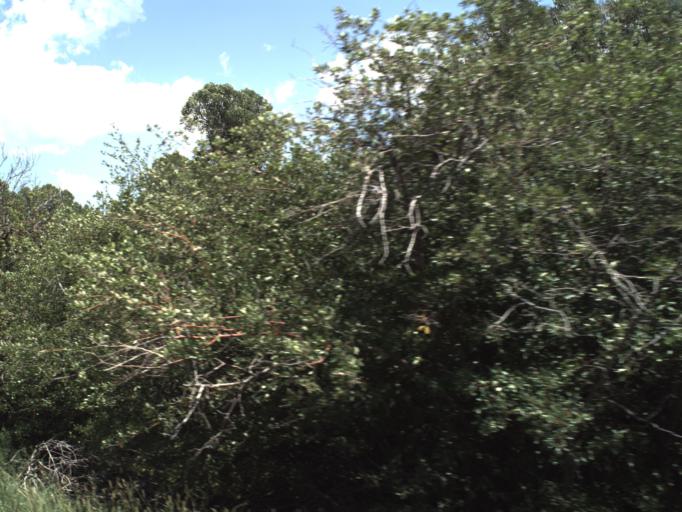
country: US
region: Utah
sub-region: Weber County
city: Wolf Creek
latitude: 41.2850
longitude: -111.6491
